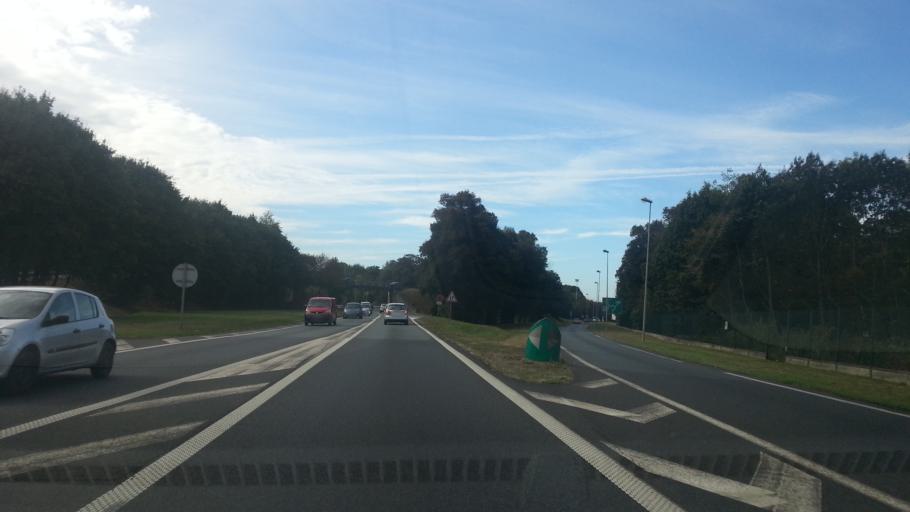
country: FR
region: Picardie
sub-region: Departement de l'Oise
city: Creil
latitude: 49.2423
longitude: 2.5114
